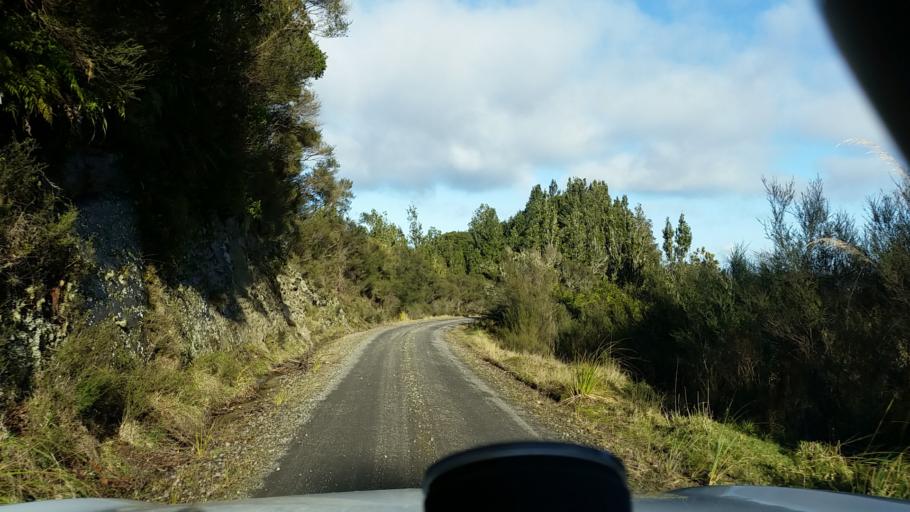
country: NZ
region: Taranaki
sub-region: South Taranaki District
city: Eltham
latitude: -39.4039
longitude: 174.5614
